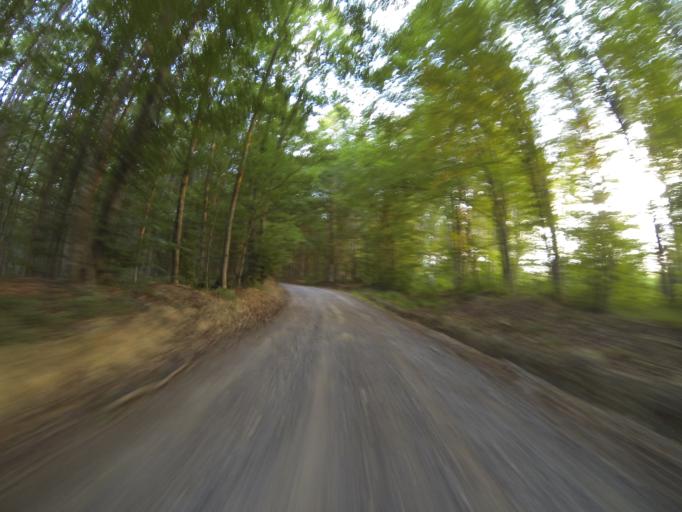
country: RO
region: Brasov
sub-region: Comuna Sinca Noua
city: Sinca Noua
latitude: 45.7237
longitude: 25.2809
